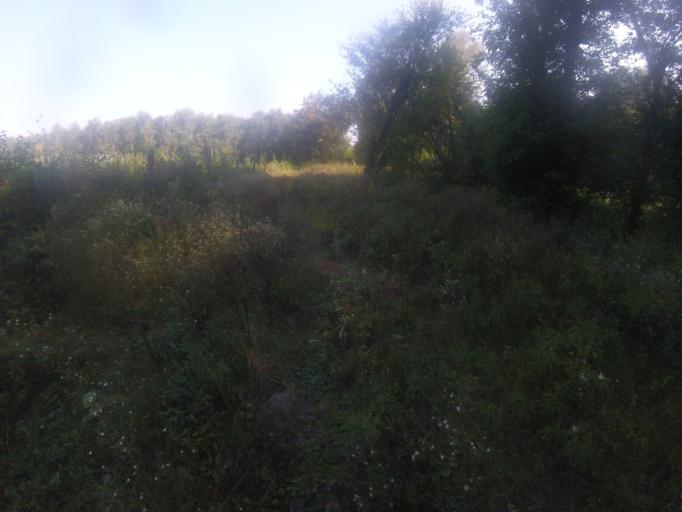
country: HU
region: Bacs-Kiskun
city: Baja
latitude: 46.1832
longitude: 18.9206
